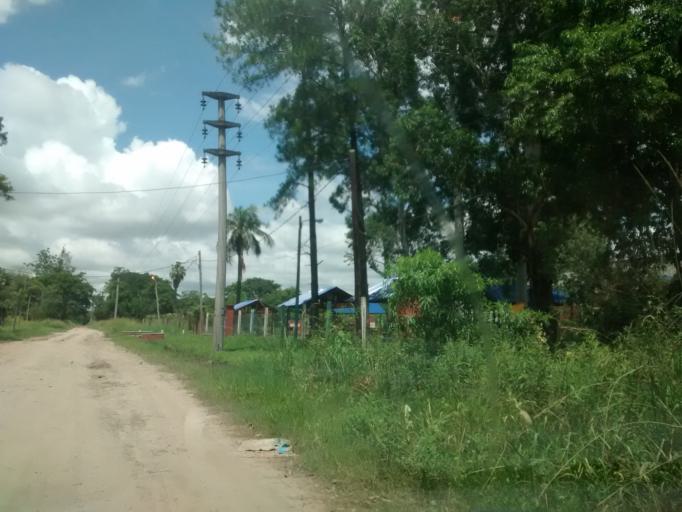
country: AR
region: Chaco
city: Fontana
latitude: -27.4099
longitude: -58.9838
